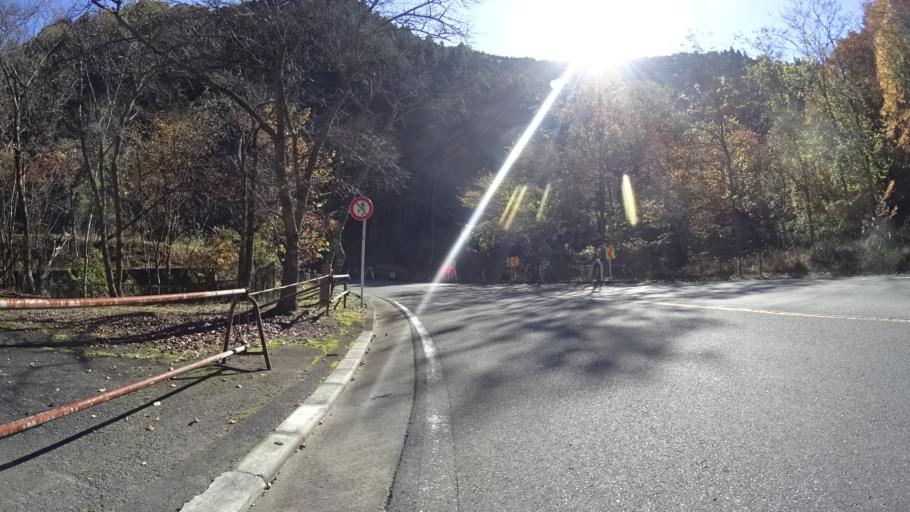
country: JP
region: Yamanashi
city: Uenohara
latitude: 35.7638
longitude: 139.0193
